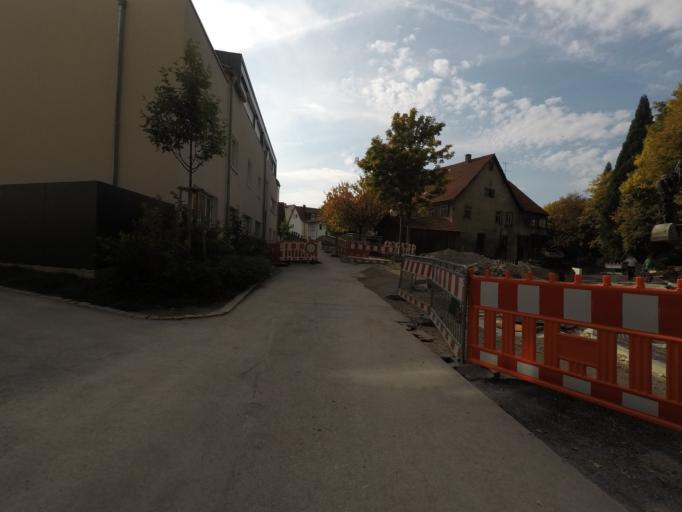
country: DE
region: Baden-Wuerttemberg
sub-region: Tuebingen Region
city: Pfullingen
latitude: 48.4615
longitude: 9.2266
